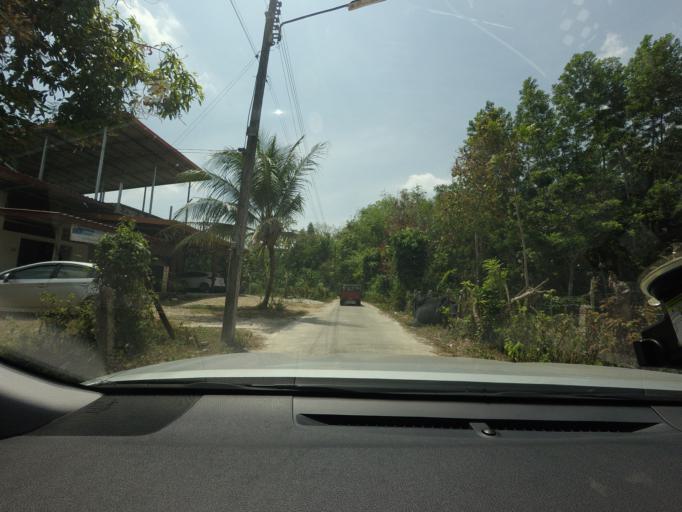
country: TH
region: Narathiwat
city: Rueso
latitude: 6.3884
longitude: 101.5092
